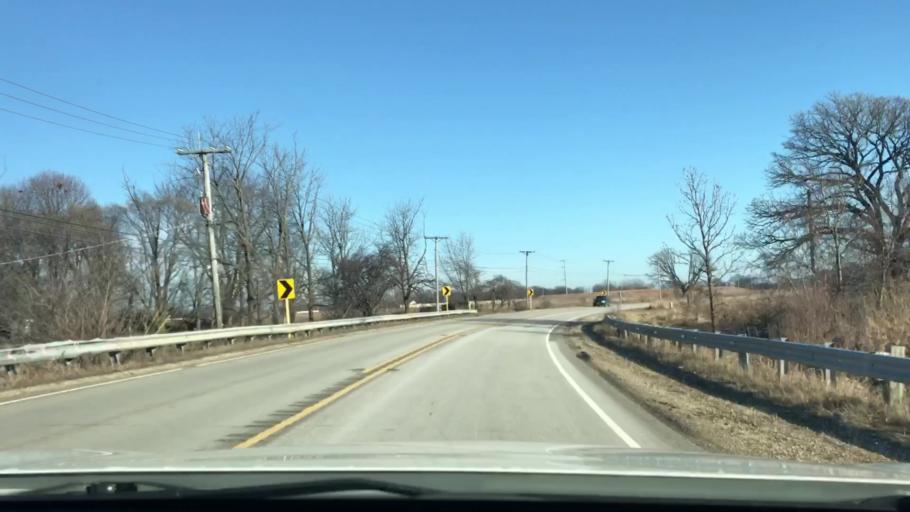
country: US
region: Illinois
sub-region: Kane County
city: Gilberts
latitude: 42.1001
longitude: -88.3949
